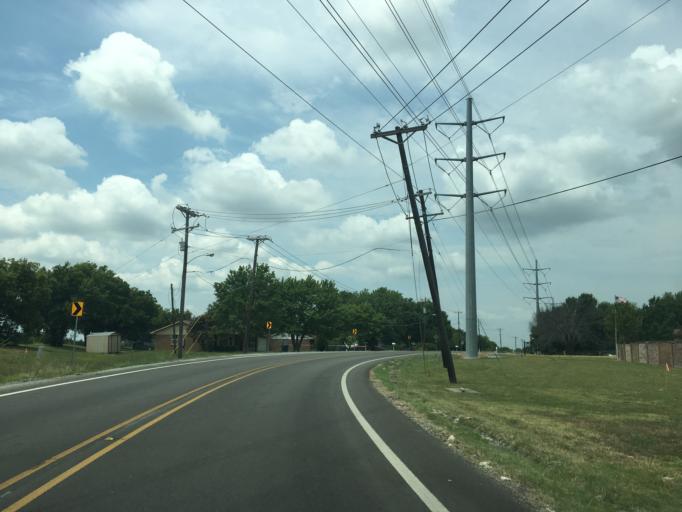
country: US
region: Texas
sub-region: Rockwall County
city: Fate
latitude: 32.9382
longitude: -96.3879
